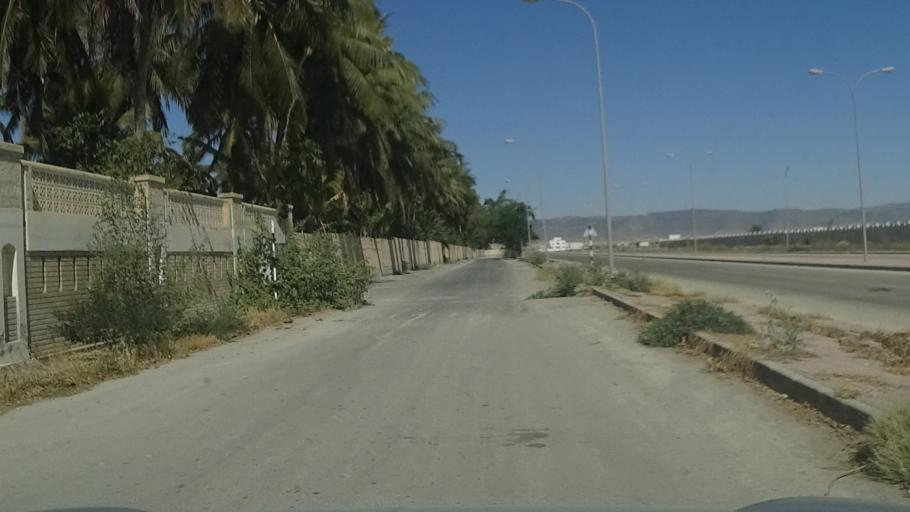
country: OM
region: Zufar
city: Salalah
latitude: 17.0269
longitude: 54.1237
